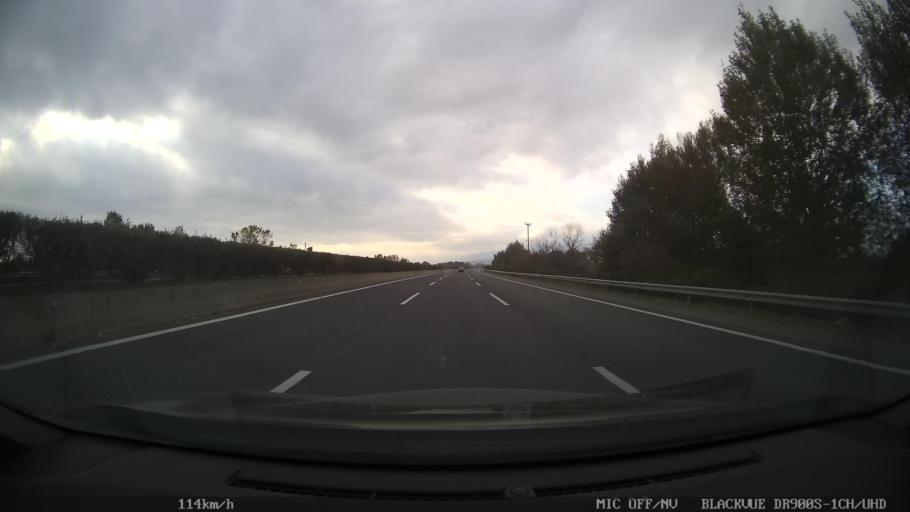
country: GR
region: Central Macedonia
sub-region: Nomos Pierias
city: Dion
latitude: 40.1809
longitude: 22.5507
